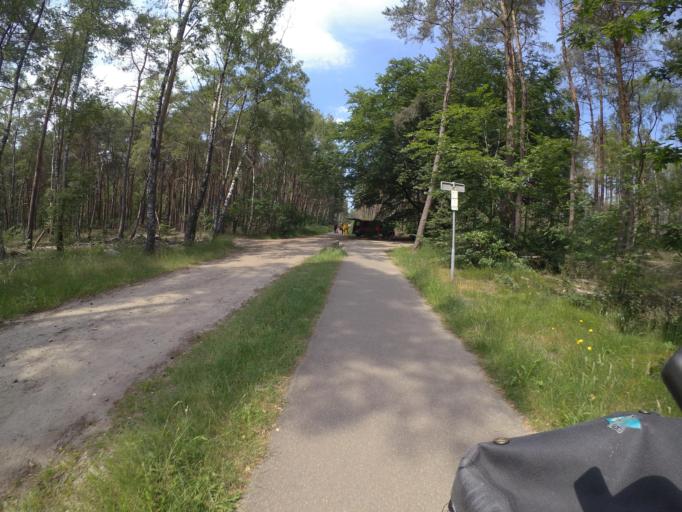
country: NL
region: Overijssel
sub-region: Gemeente Twenterand
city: Den Ham
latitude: 52.3827
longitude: 6.4335
